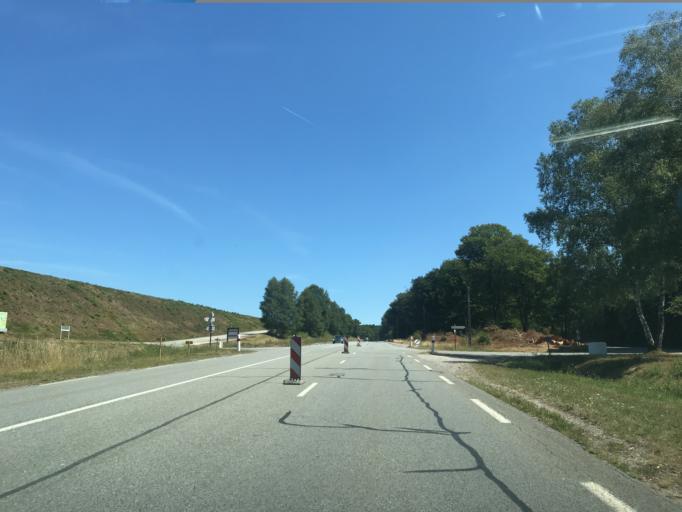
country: FR
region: Limousin
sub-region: Departement de la Correze
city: Egletons
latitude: 45.4186
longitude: 2.0633
